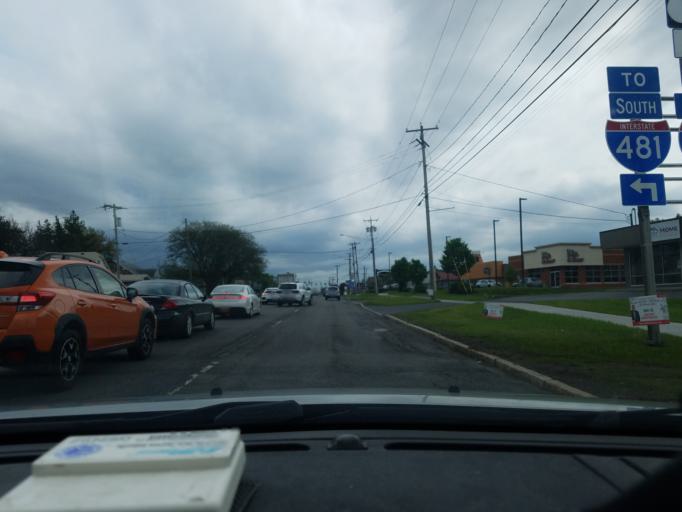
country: US
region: New York
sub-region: Onondaga County
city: North Syracuse
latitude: 43.1468
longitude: -76.1265
